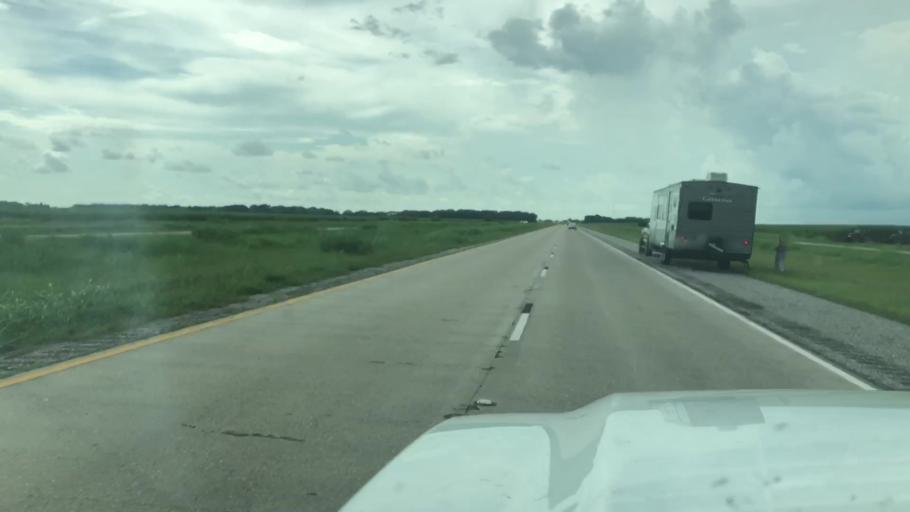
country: US
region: Louisiana
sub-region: Saint Mary Parish
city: Baldwin
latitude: 29.8496
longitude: -91.5948
